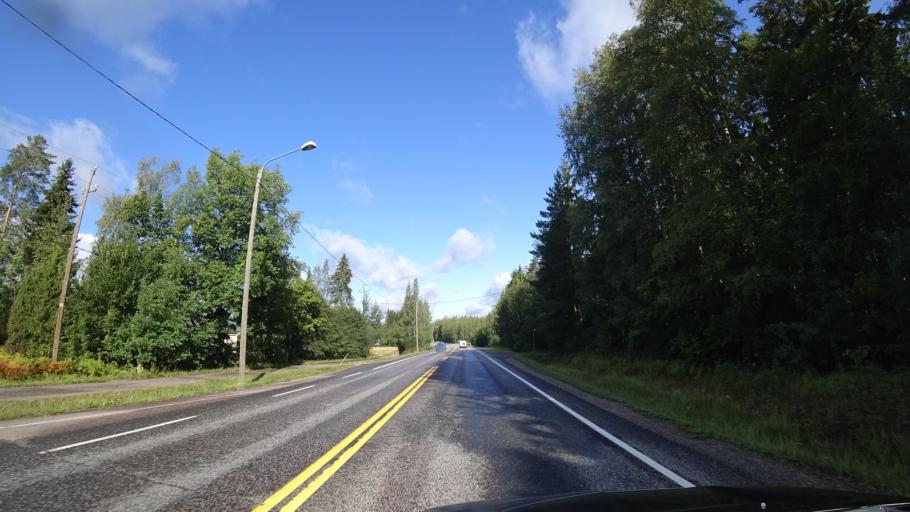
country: FI
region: Uusimaa
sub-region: Helsinki
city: Tuusula
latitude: 60.4418
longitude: 24.9757
